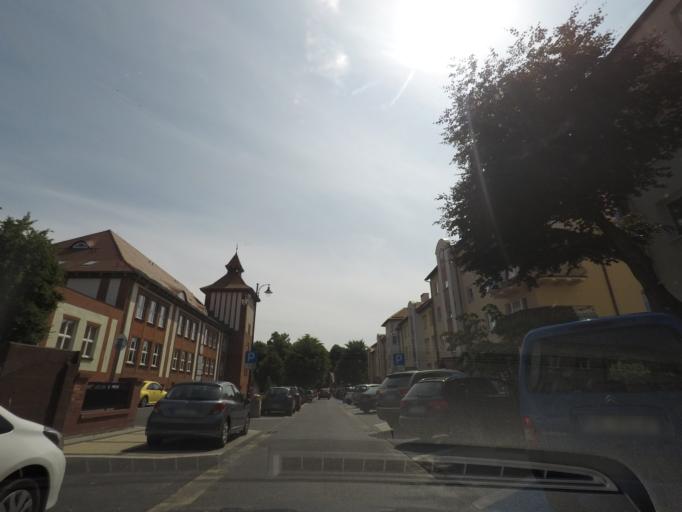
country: PL
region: Pomeranian Voivodeship
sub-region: Powiat slupski
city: Ustka
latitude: 54.5837
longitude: 16.8604
